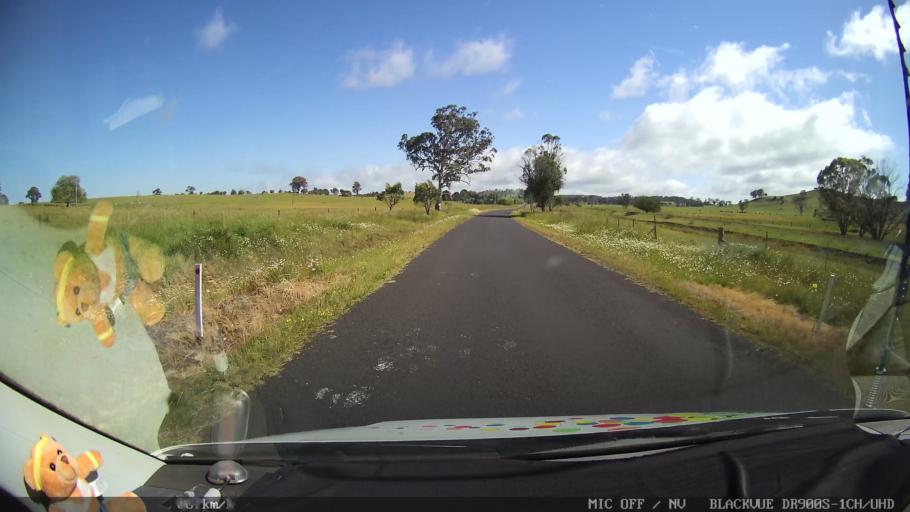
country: AU
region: New South Wales
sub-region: Guyra
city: Guyra
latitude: -30.0582
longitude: 151.6650
